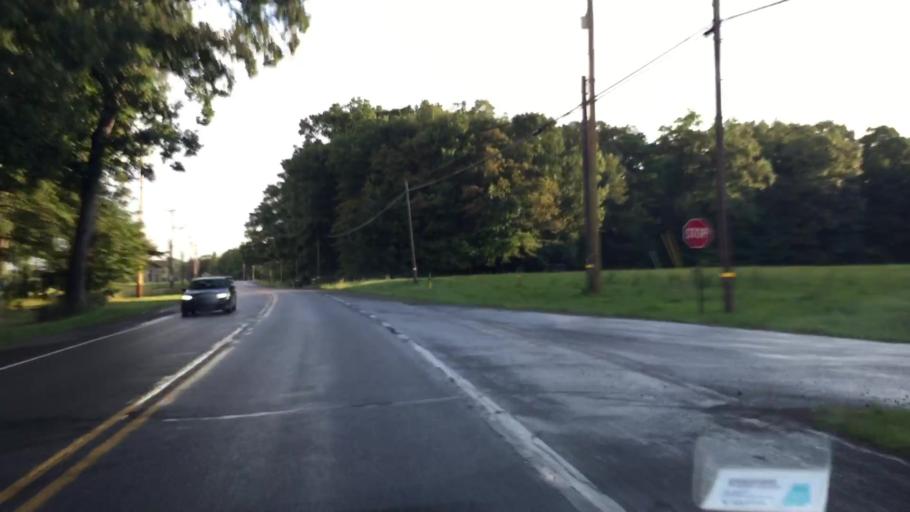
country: US
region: Pennsylvania
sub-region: Butler County
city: Meridian
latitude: 40.8285
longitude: -80.0098
